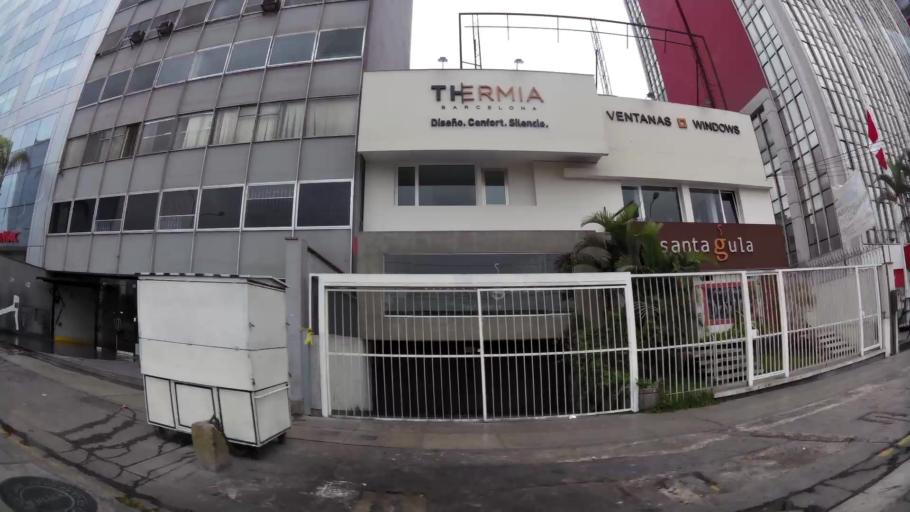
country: PE
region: Lima
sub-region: Lima
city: San Isidro
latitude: -12.0999
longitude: -77.0261
